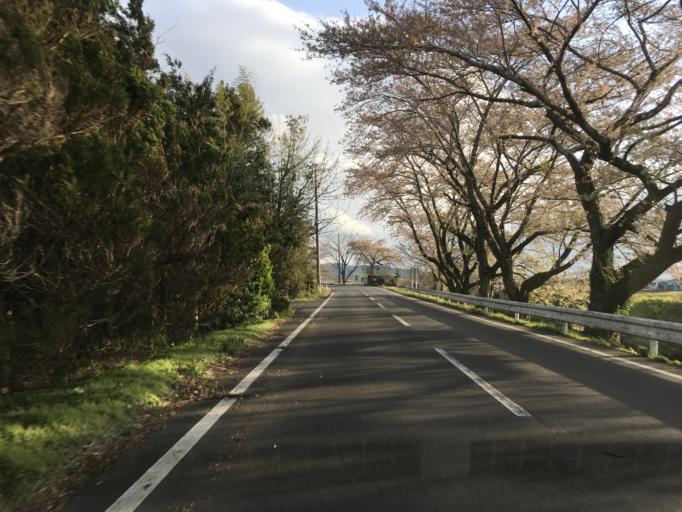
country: JP
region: Miyagi
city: Wakuya
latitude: 38.6510
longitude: 141.1448
